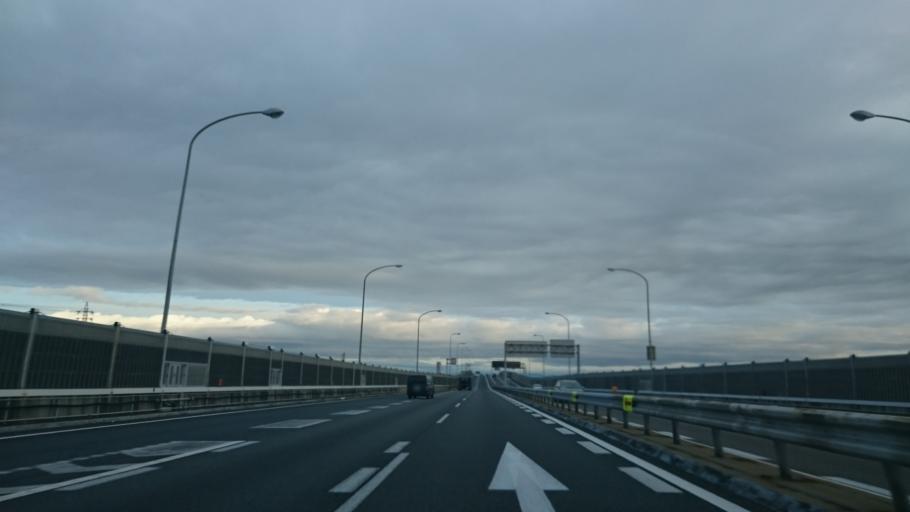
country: JP
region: Aichi
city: Kanie
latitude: 35.1652
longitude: 136.8171
